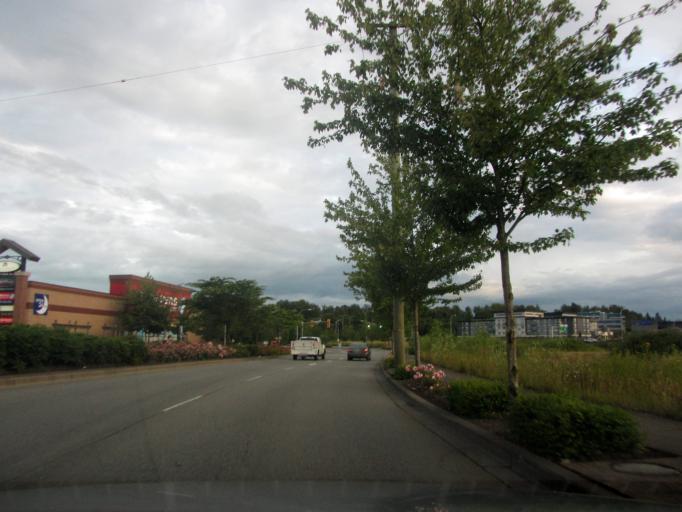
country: CA
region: British Columbia
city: Walnut Grove
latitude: 49.1656
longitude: -122.6663
